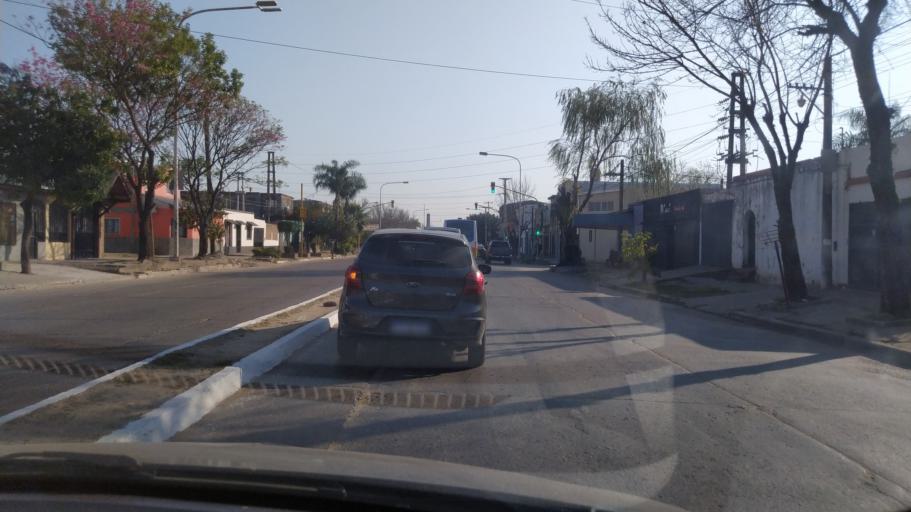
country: AR
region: Corrientes
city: Corrientes
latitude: -27.4815
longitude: -58.8153
